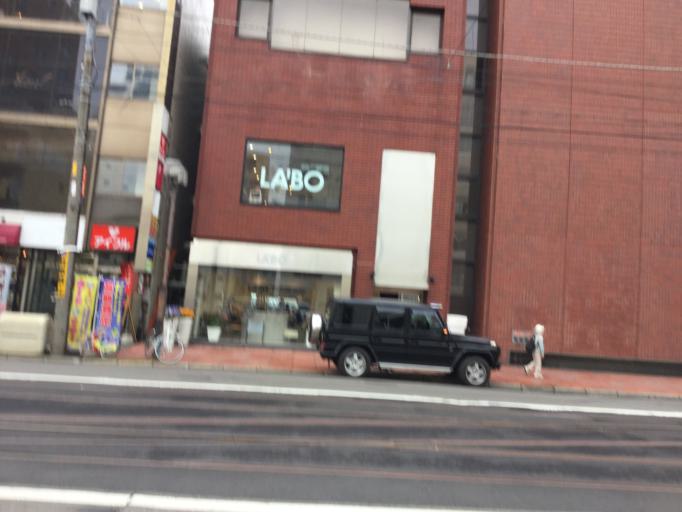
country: JP
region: Hokkaido
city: Sapporo
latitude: 43.0587
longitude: 141.3504
